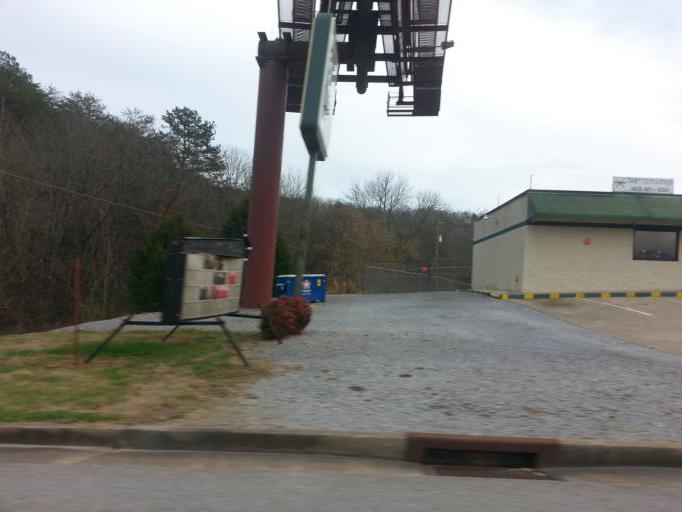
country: US
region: Tennessee
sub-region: Hamilton County
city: Sale Creek
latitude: 35.3667
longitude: -85.1178
